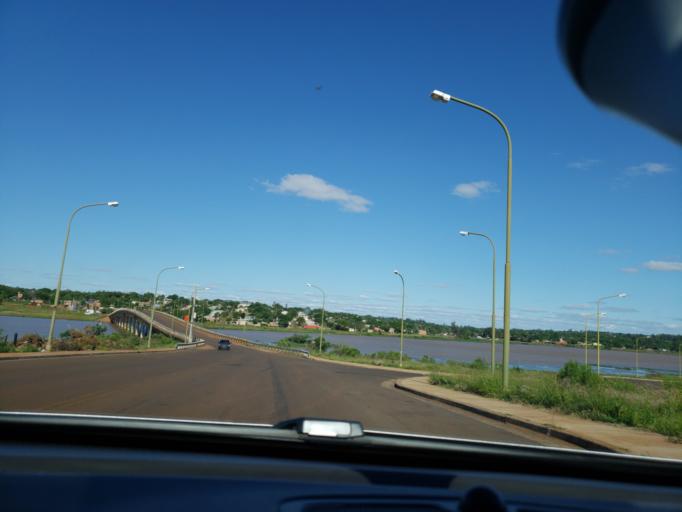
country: AR
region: Misiones
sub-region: Departamento de Capital
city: Posadas
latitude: -27.3825
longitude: -55.9580
